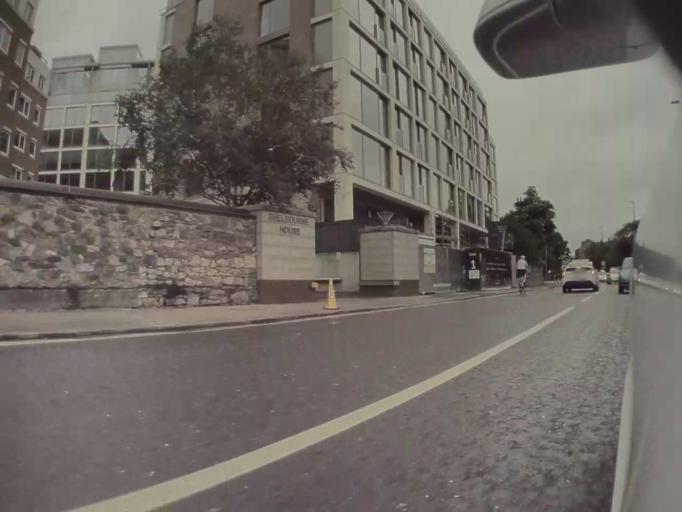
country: IE
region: Leinster
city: Ringsend
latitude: 53.3326
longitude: -6.2317
